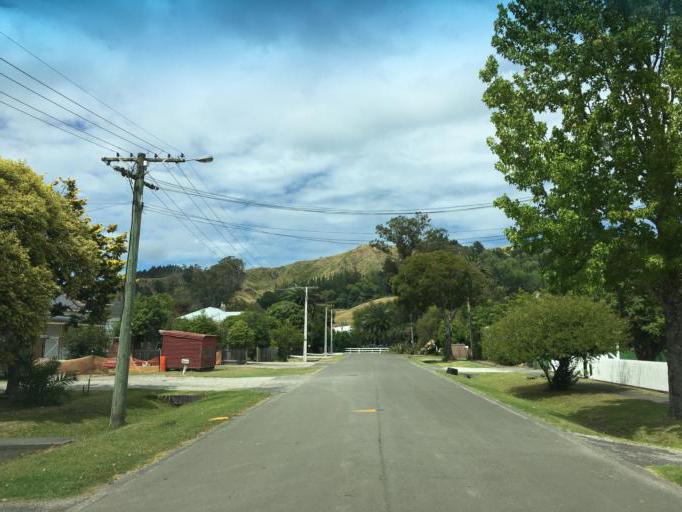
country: NZ
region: Gisborne
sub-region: Gisborne District
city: Gisborne
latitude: -38.6714
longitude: 178.0341
